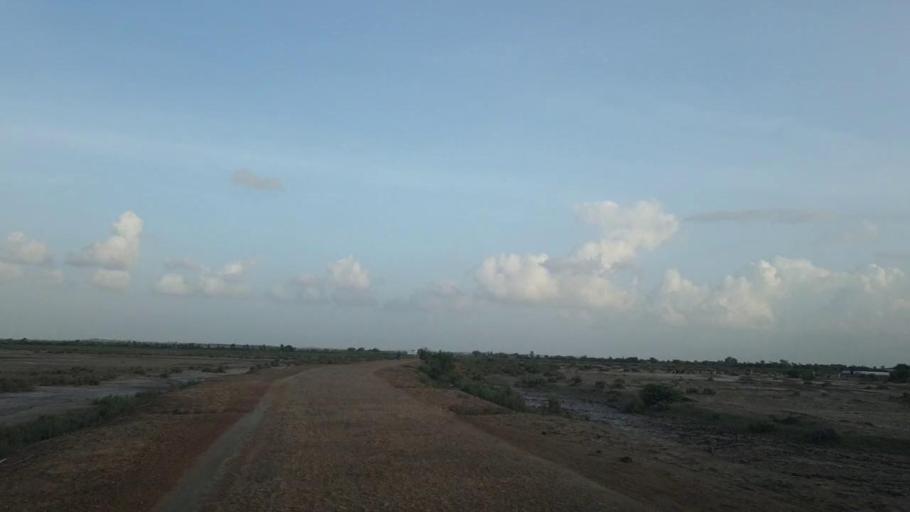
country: PK
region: Sindh
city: Kadhan
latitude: 24.5546
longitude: 69.1230
